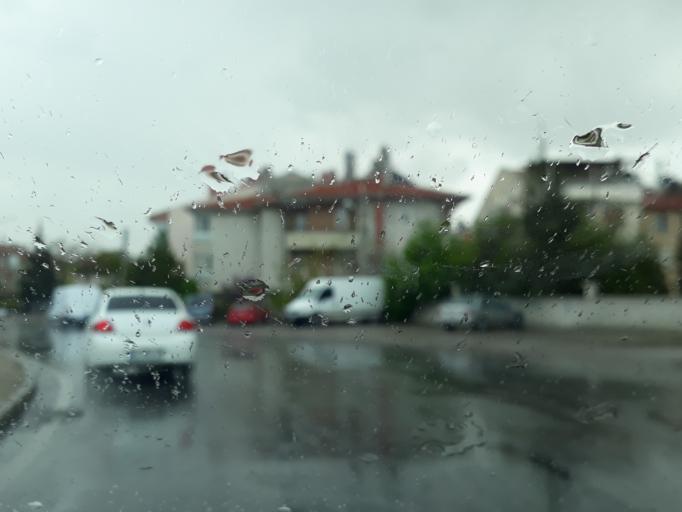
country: TR
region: Konya
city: Selcuklu
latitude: 37.9153
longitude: 32.4923
